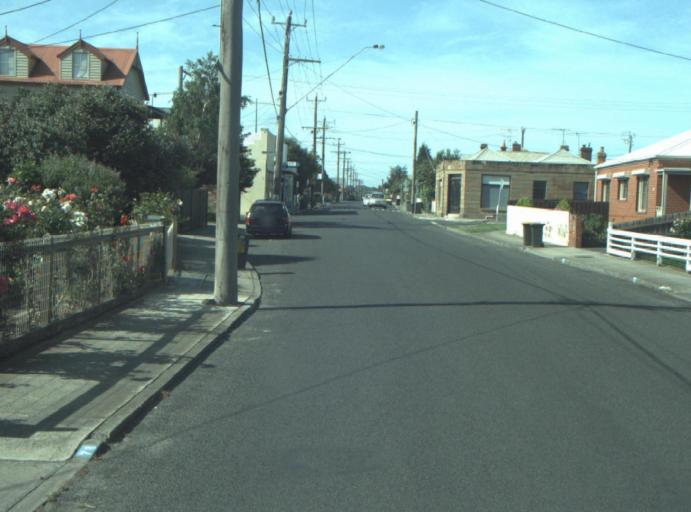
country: AU
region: Victoria
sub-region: Greater Geelong
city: Geelong West
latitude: -38.1363
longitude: 144.3407
